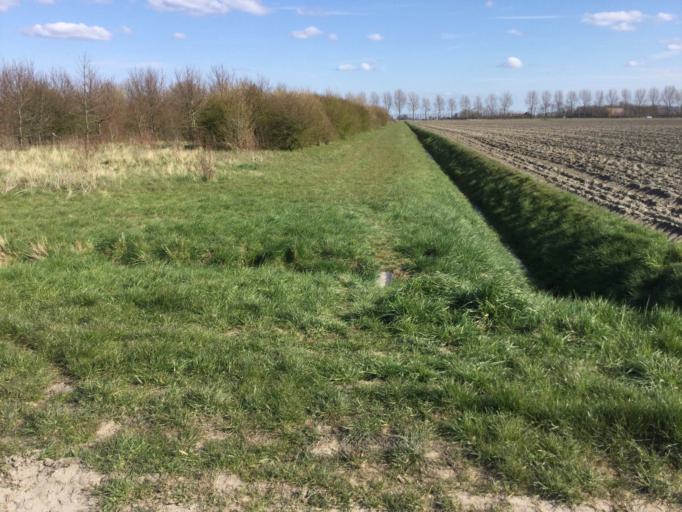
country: NL
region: South Holland
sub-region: Gemeente Lisse
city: Lisse
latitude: 52.2627
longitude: 4.5819
